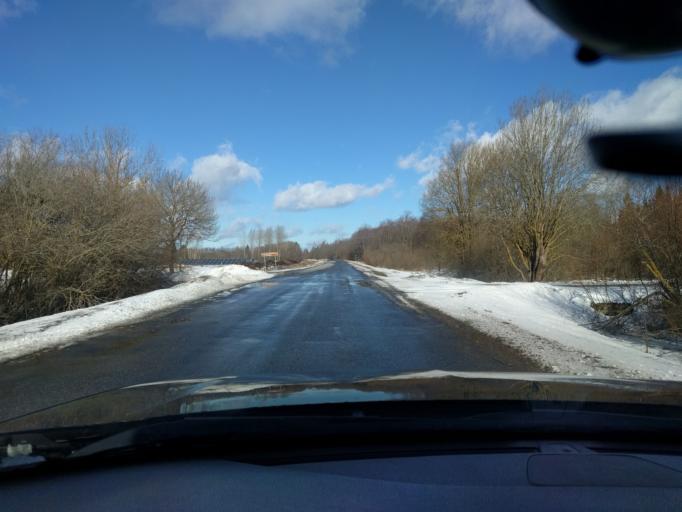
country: EE
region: Harju
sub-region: Raasiku vald
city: Raasiku
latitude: 59.3010
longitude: 25.1726
